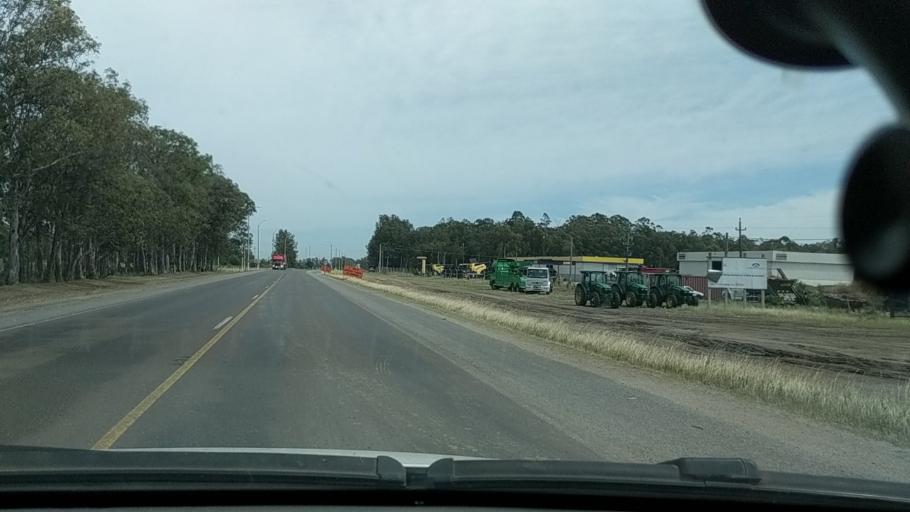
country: UY
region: Durazno
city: Durazno
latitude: -33.4152
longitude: -56.5087
